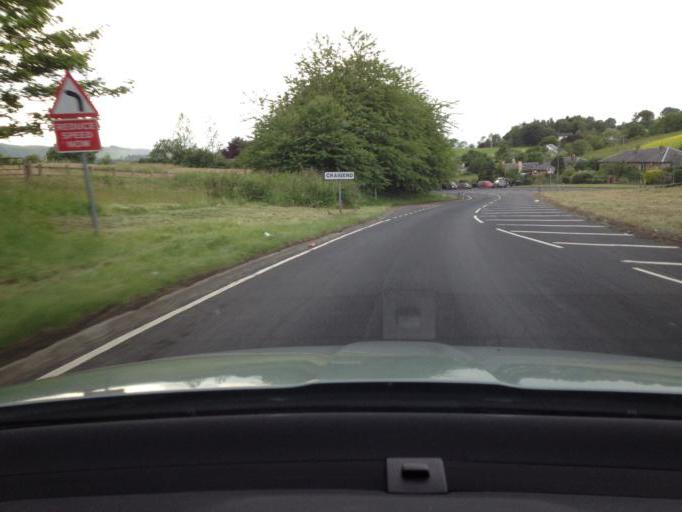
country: GB
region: Scotland
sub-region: Perth and Kinross
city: Bridge of Earn
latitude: 56.3672
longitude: -3.4246
